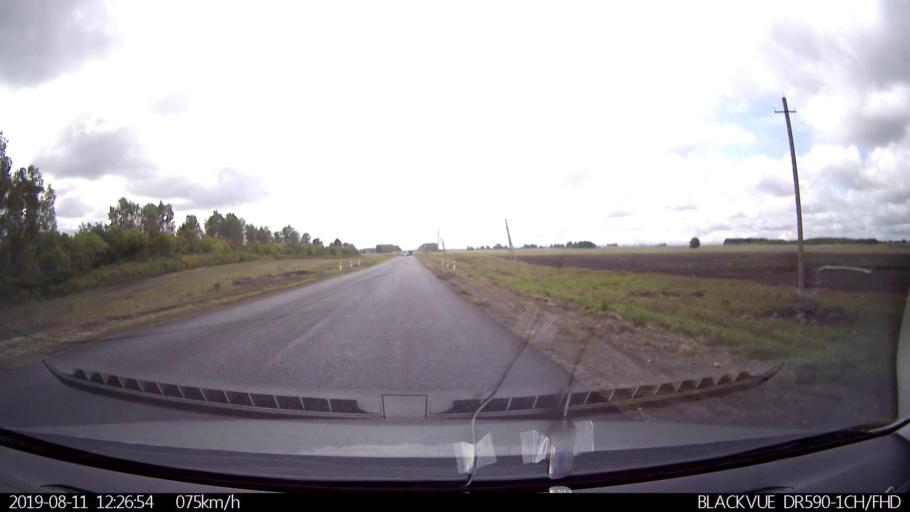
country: RU
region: Ulyanovsk
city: Ignatovka
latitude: 53.8607
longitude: 47.9278
